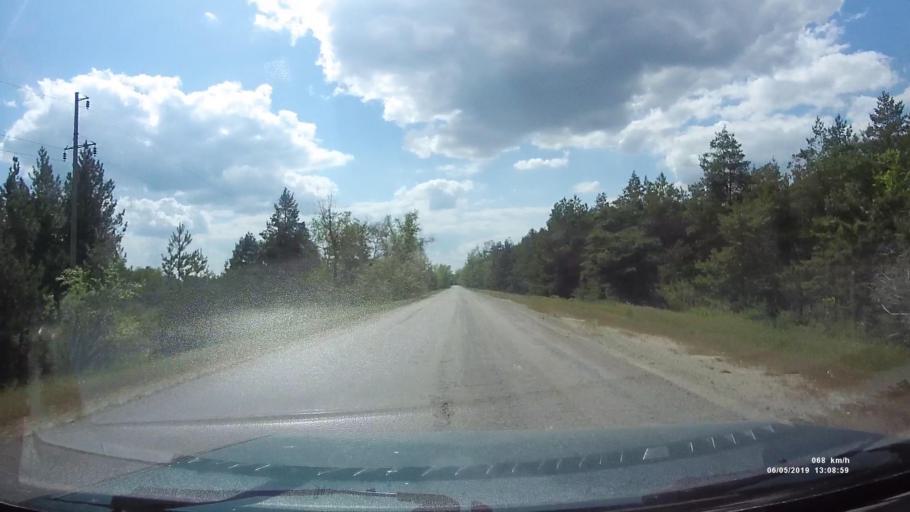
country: RU
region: Rostov
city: Ust'-Donetskiy
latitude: 47.7719
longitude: 40.9895
